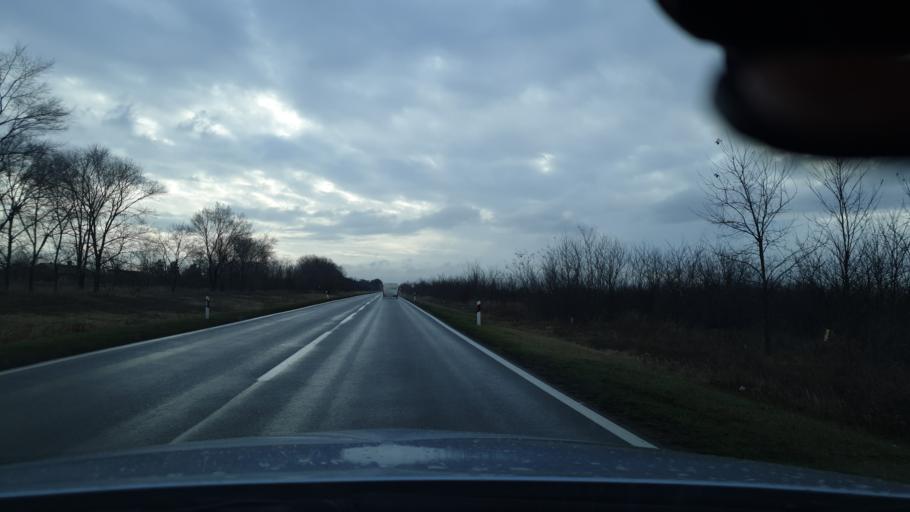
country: RS
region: Autonomna Pokrajina Vojvodina
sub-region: Juznobanatski Okrug
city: Kovin
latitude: 44.7667
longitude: 20.9500
